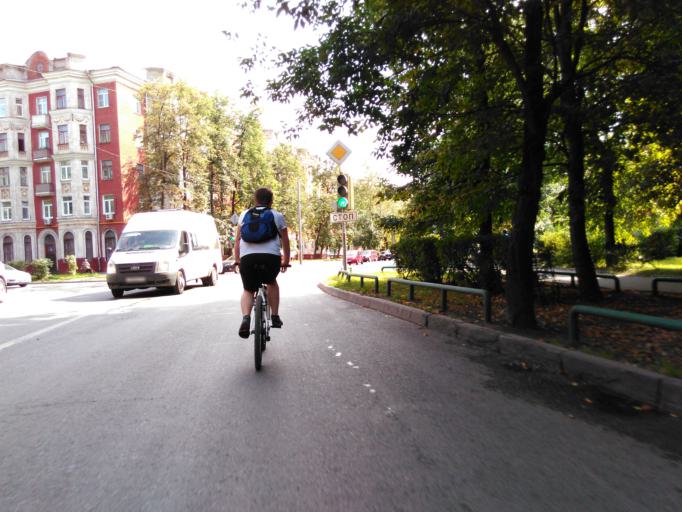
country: RU
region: Moskovskaya
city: Bol'shaya Setun'
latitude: 55.7232
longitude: 37.4005
